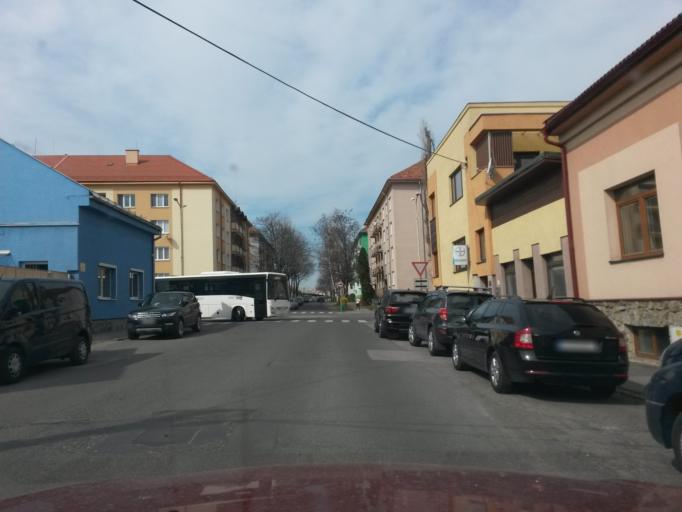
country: SK
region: Banskobystricky
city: Lucenec
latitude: 48.3355
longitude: 19.6650
